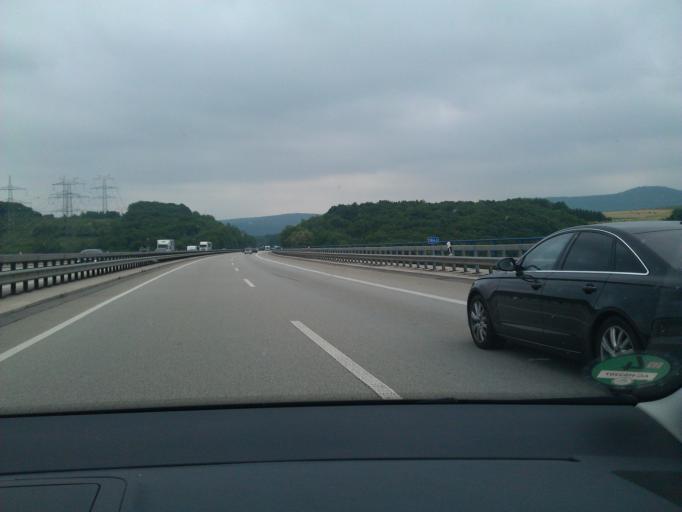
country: DE
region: Rheinland-Pfalz
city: Bad Neuenahr-Ahrweiler
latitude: 50.5657
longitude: 7.1445
